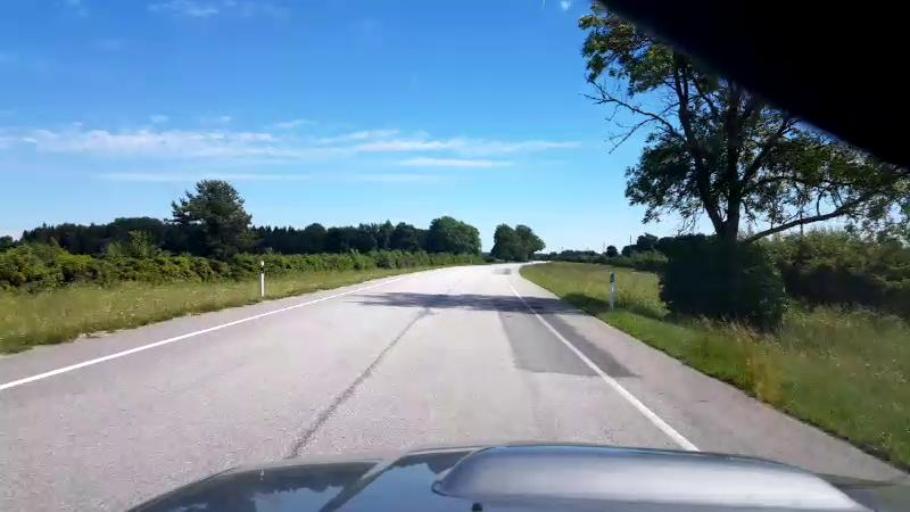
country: EE
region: Jaervamaa
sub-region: Koeru vald
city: Koeru
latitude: 58.9907
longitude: 25.9680
